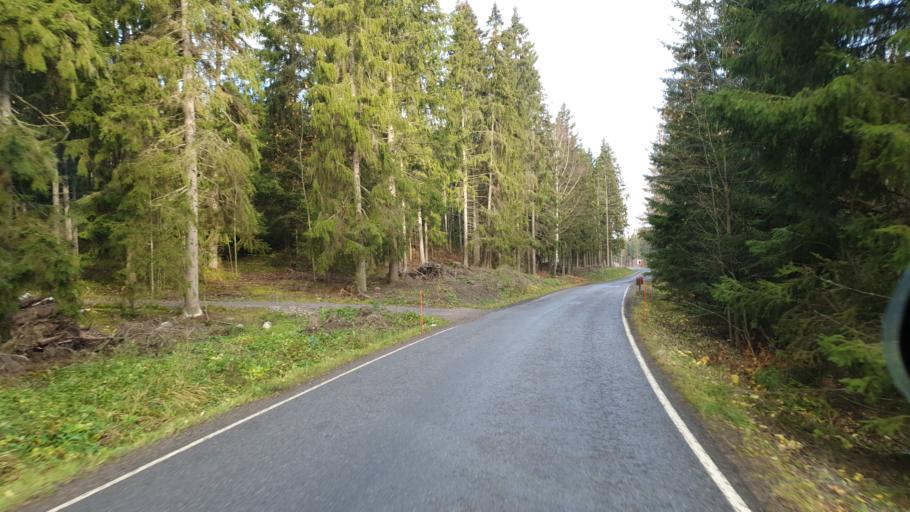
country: FI
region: Uusimaa
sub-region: Helsinki
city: Siuntio
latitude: 60.2637
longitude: 24.3029
